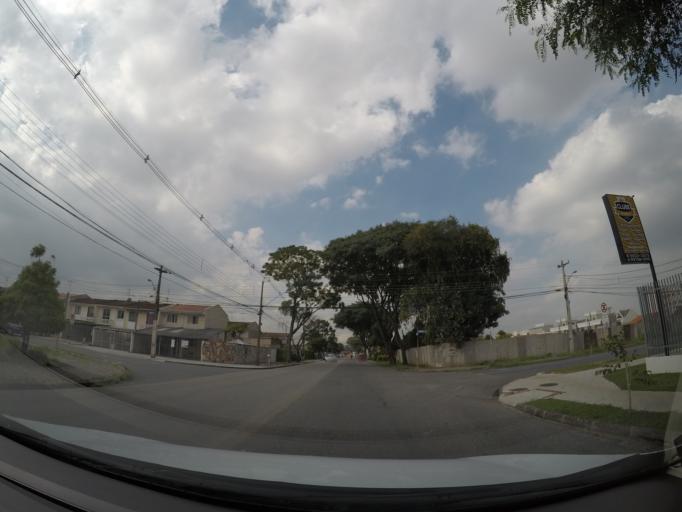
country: BR
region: Parana
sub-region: Curitiba
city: Curitiba
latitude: -25.4848
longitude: -49.2514
